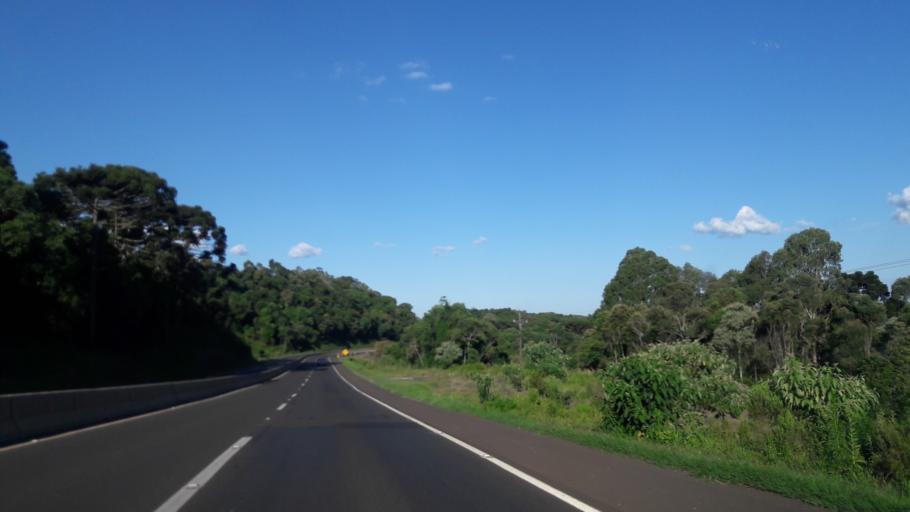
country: BR
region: Parana
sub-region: Guarapuava
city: Guarapuava
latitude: -25.3478
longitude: -51.3884
